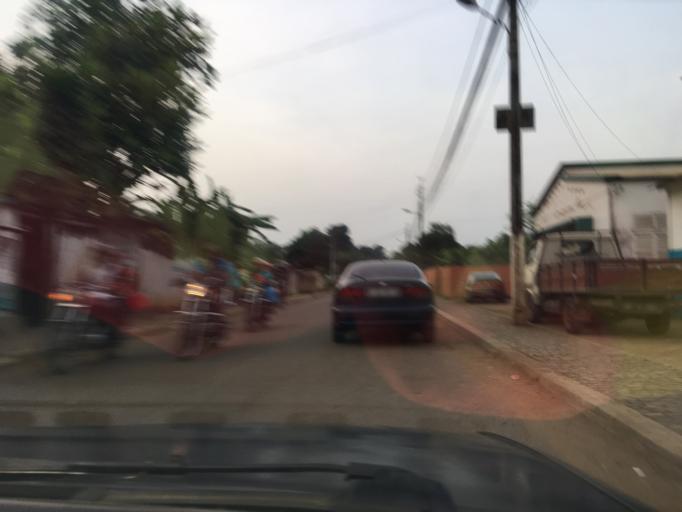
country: ST
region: Sao Tome Island
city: Sao Tome
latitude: 0.3164
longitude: 6.7293
